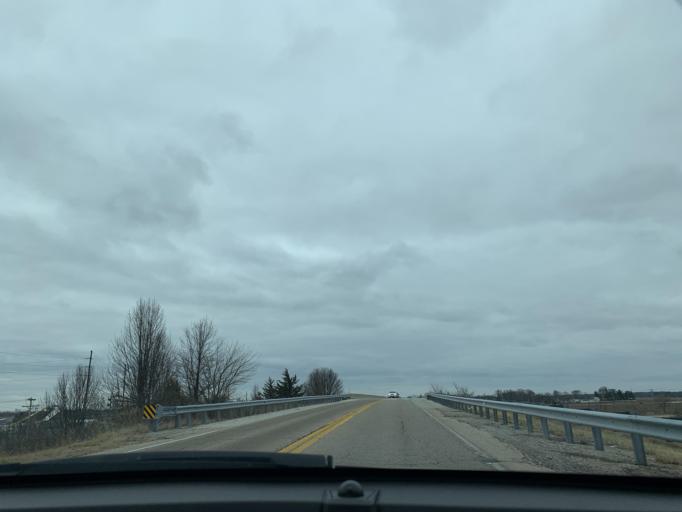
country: US
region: Illinois
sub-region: Sangamon County
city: Jerome
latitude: 39.7438
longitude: -89.6868
